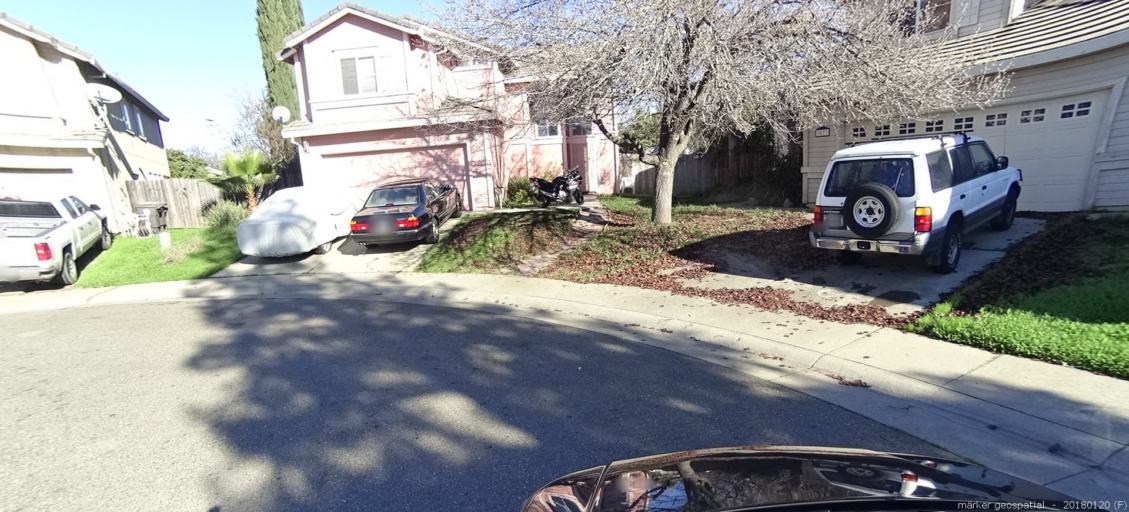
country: US
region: California
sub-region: Sacramento County
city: Rancho Cordova
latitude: 38.5683
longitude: -121.3132
